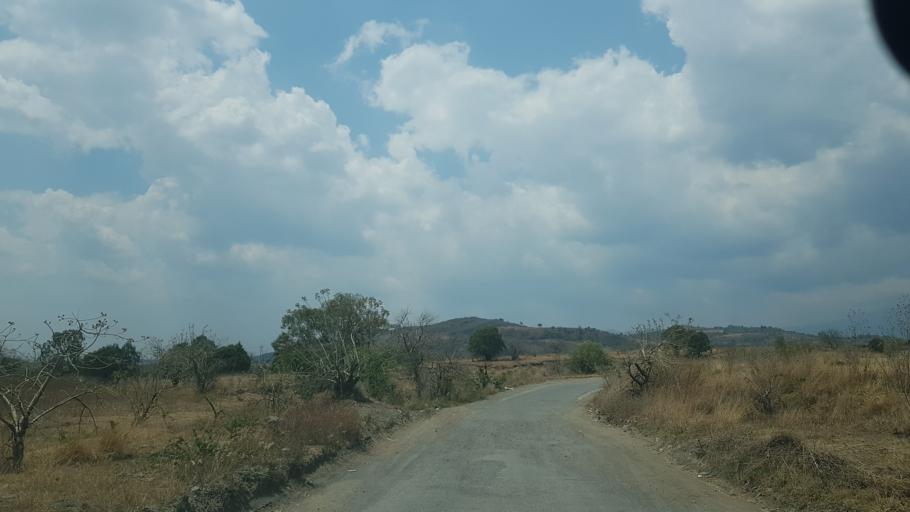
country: MX
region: Puebla
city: San Juan Amecac
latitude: 18.8268
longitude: -98.6223
